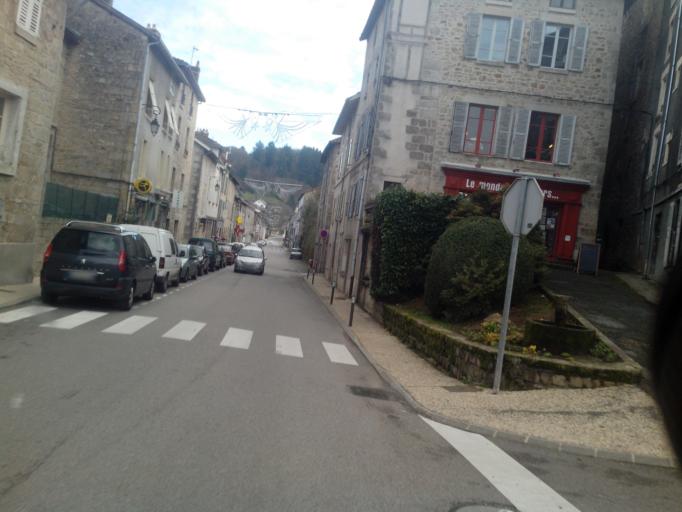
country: FR
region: Limousin
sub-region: Departement de la Haute-Vienne
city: Eymoutiers
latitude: 45.7388
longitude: 1.7434
